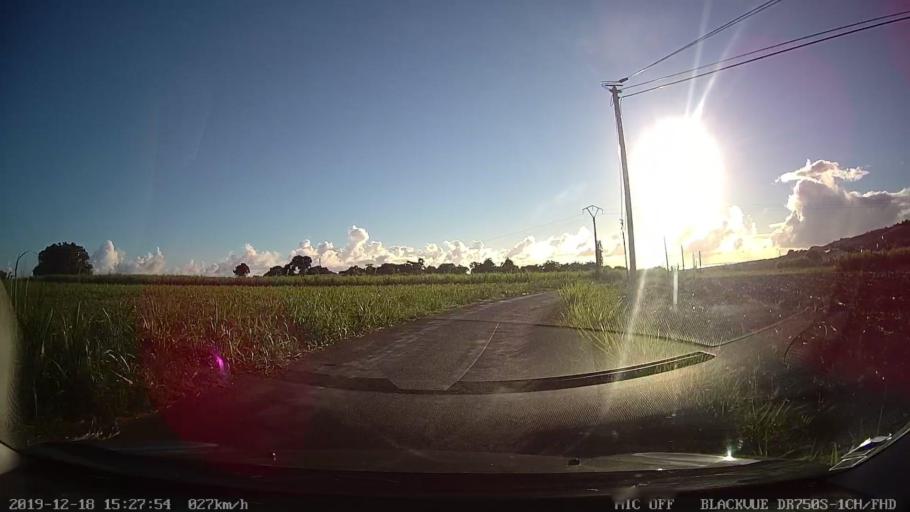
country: RE
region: Reunion
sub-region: Reunion
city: Bras-Panon
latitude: -20.9989
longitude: 55.6553
